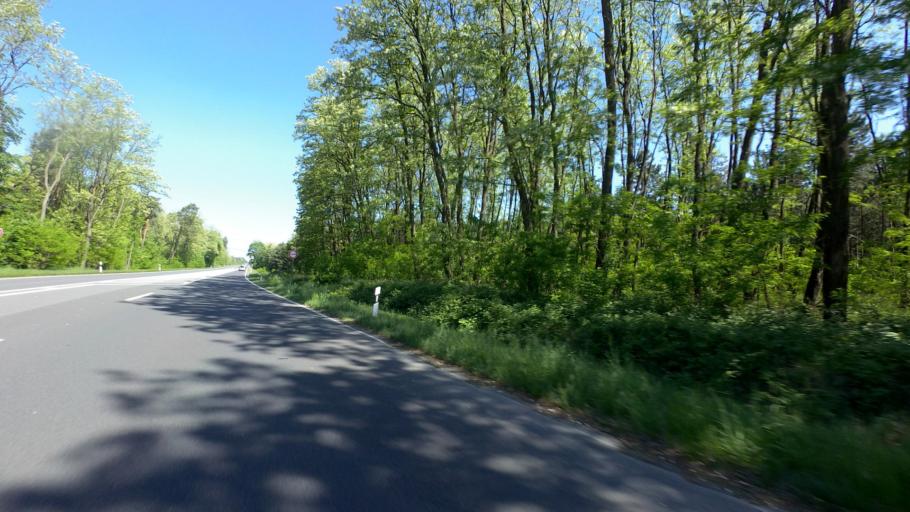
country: DE
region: Brandenburg
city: Spremberg
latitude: 51.6212
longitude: 14.3628
